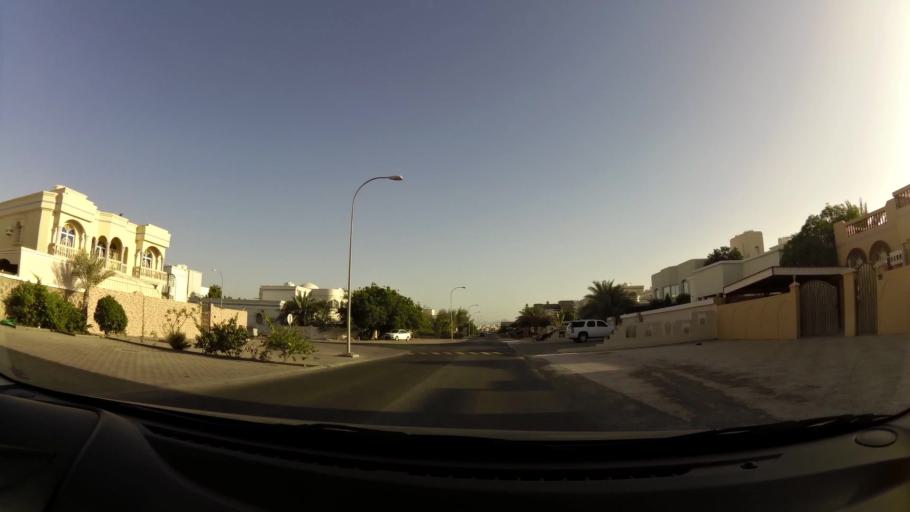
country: OM
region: Muhafazat Masqat
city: As Sib al Jadidah
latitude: 23.6107
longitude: 58.2201
